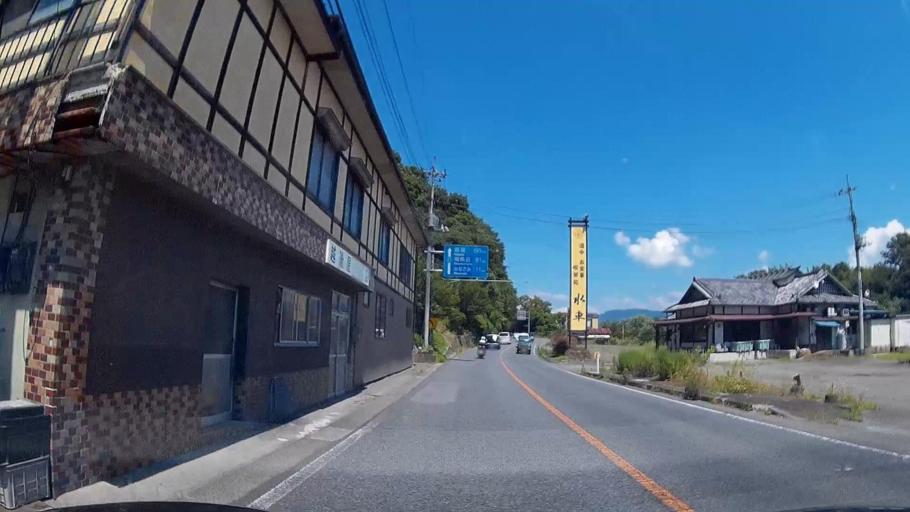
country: JP
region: Gunma
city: Numata
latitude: 36.6056
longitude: 139.0454
